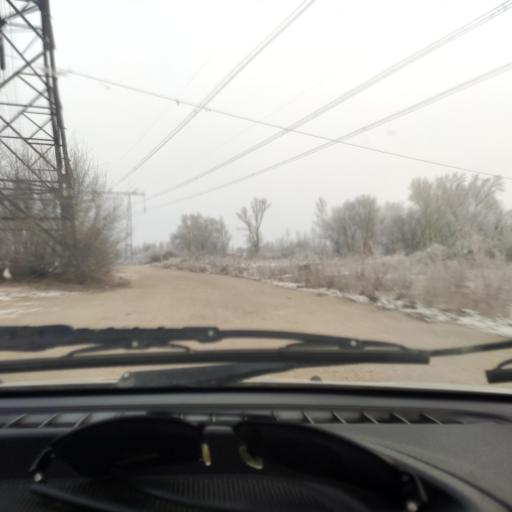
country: RU
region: Samara
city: Zhigulevsk
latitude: 53.4775
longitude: 49.5052
